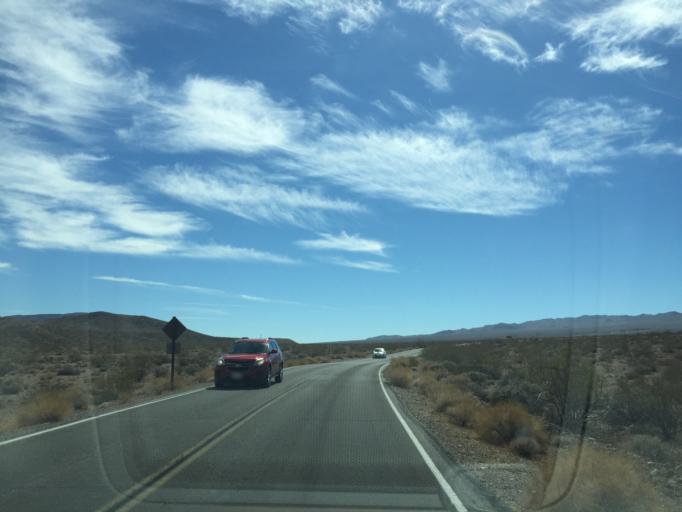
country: US
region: Nevada
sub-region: Nye County
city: Beatty
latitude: 36.2728
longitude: -116.6638
